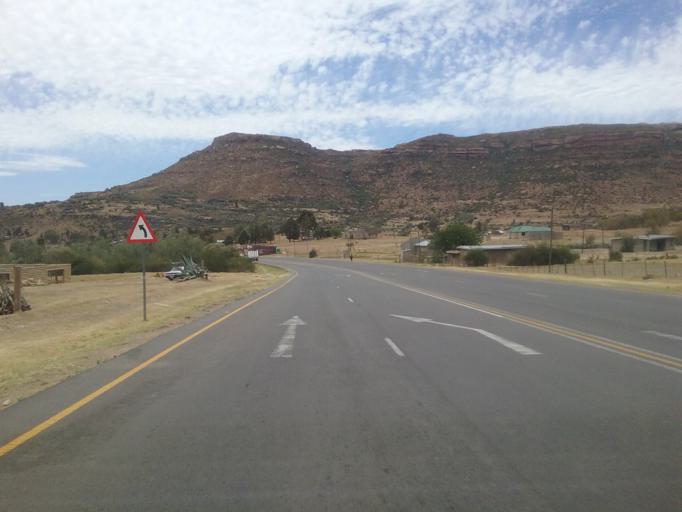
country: LS
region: Mafeteng
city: Mafeteng
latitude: -29.6450
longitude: 27.4717
